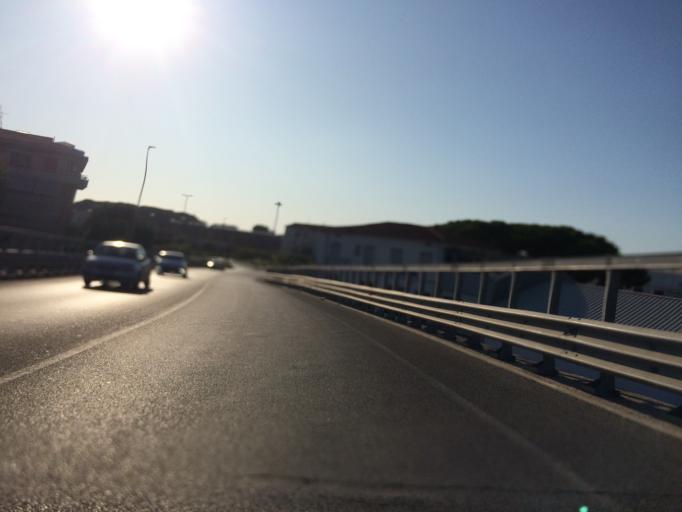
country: IT
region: Tuscany
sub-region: Provincia di Lucca
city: Viareggio
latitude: 43.8624
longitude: 10.2602
